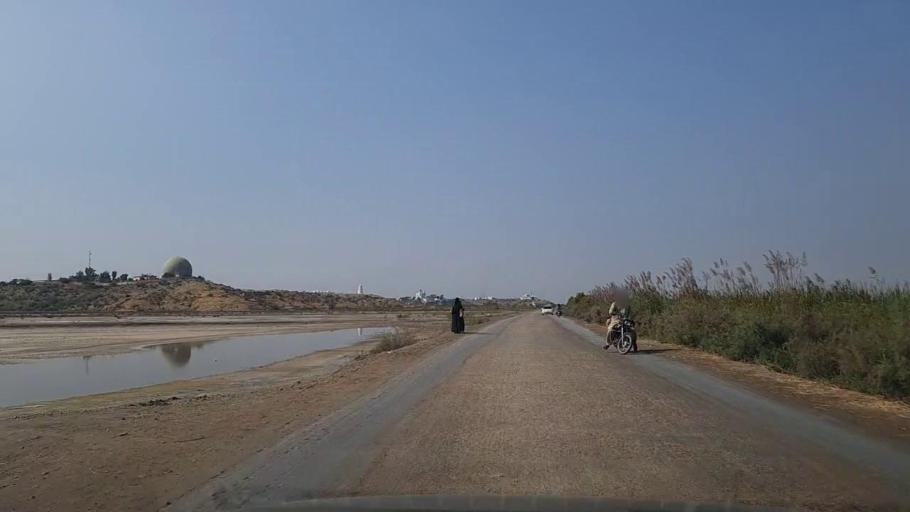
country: PK
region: Sindh
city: Chuhar Jamali
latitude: 24.5515
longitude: 67.8928
